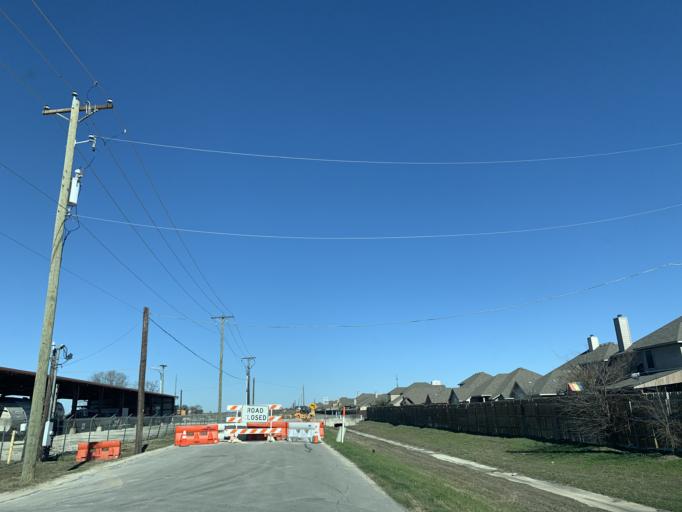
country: US
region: Texas
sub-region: Williamson County
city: Hutto
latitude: 30.5466
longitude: -97.5660
